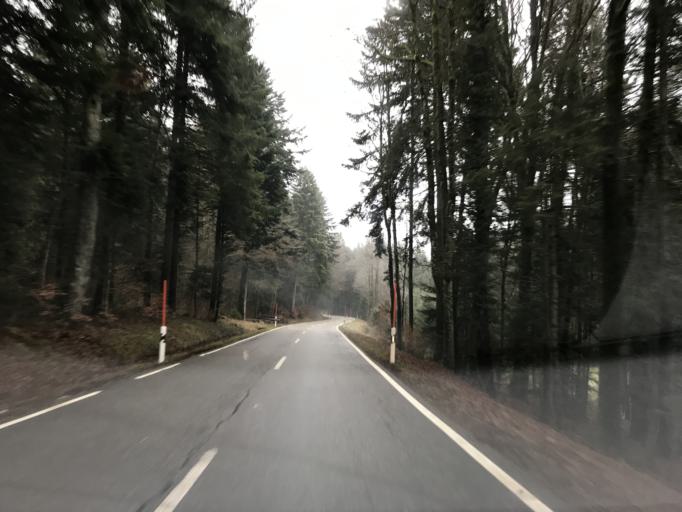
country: DE
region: Baden-Wuerttemberg
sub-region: Freiburg Region
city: Rickenbach
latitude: 47.6136
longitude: 7.9699
